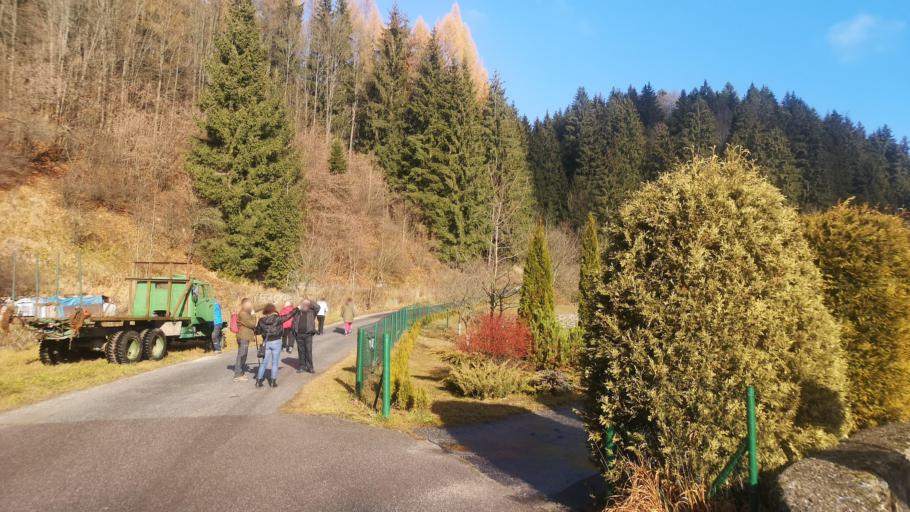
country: SK
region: Banskobystricky
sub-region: Okres Ziar nad Hronom
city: Kremnica
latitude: 48.7594
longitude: 18.9268
